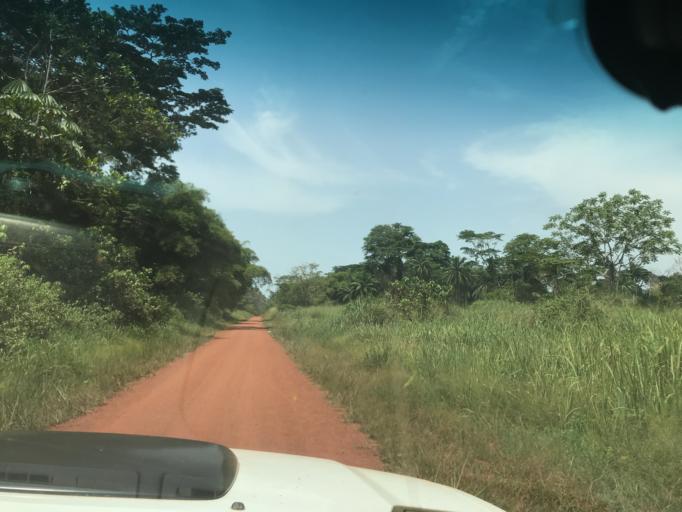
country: CD
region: Eastern Province
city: Aketi
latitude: 2.8748
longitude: 23.9555
